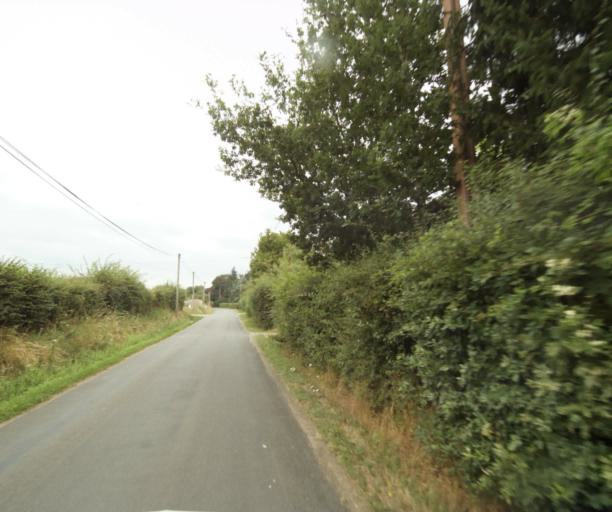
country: FR
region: Pays de la Loire
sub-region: Departement de la Sarthe
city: Juigne-sur-Sarthe
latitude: 47.8563
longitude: -0.2890
